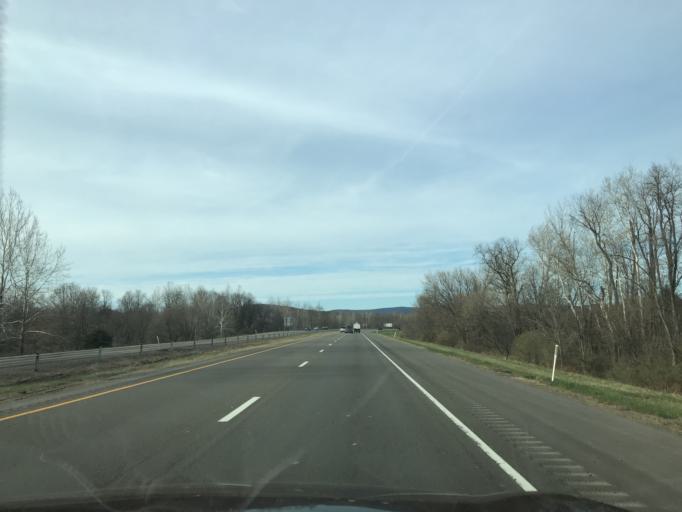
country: US
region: Pennsylvania
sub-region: Lycoming County
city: Montoursville
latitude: 41.2565
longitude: -76.9302
